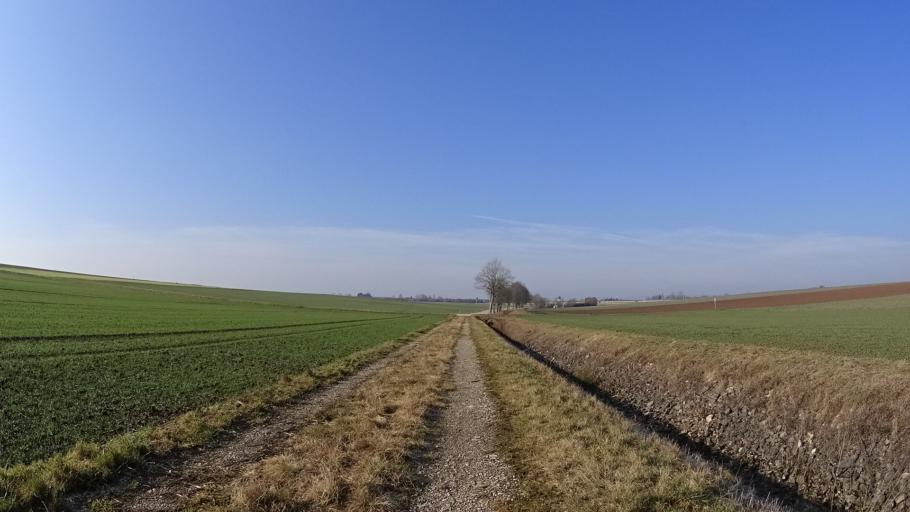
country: DE
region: Bavaria
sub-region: Upper Bavaria
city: Stammham
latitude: 48.8686
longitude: 11.4786
